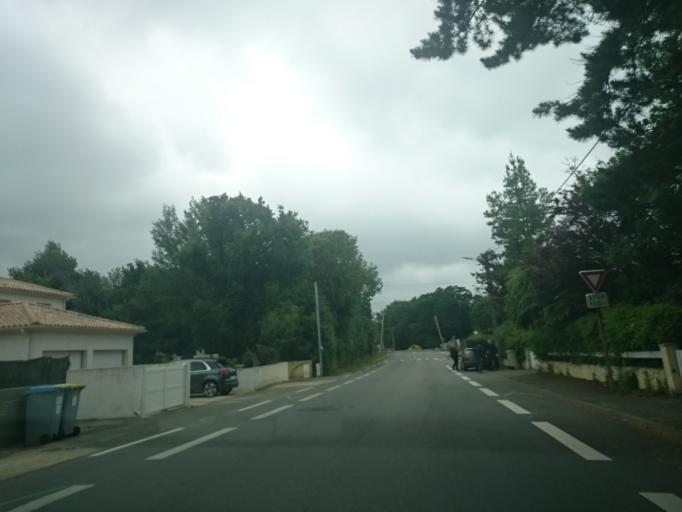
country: FR
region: Pays de la Loire
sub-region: Departement de la Loire-Atlantique
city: Bouaye
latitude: 47.1386
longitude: -1.6730
